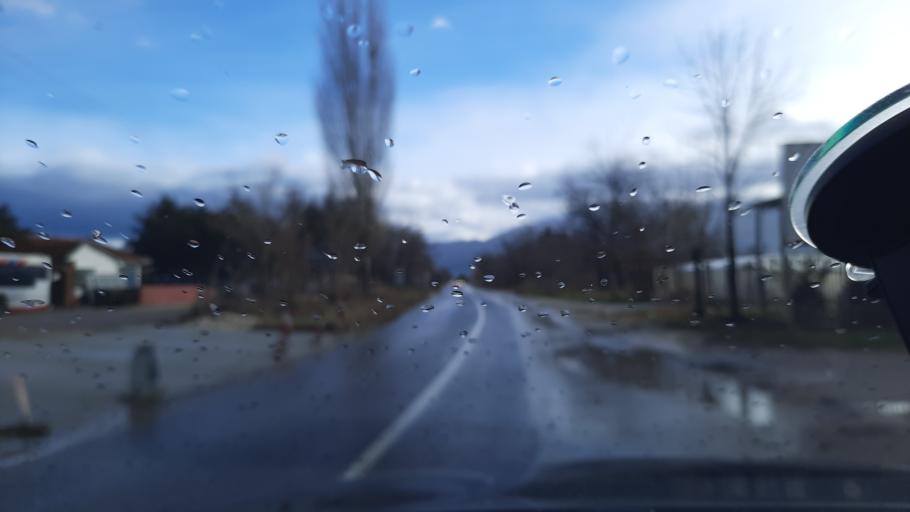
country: MK
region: Prilep
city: Markov Grad
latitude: 41.3430
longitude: 21.5206
